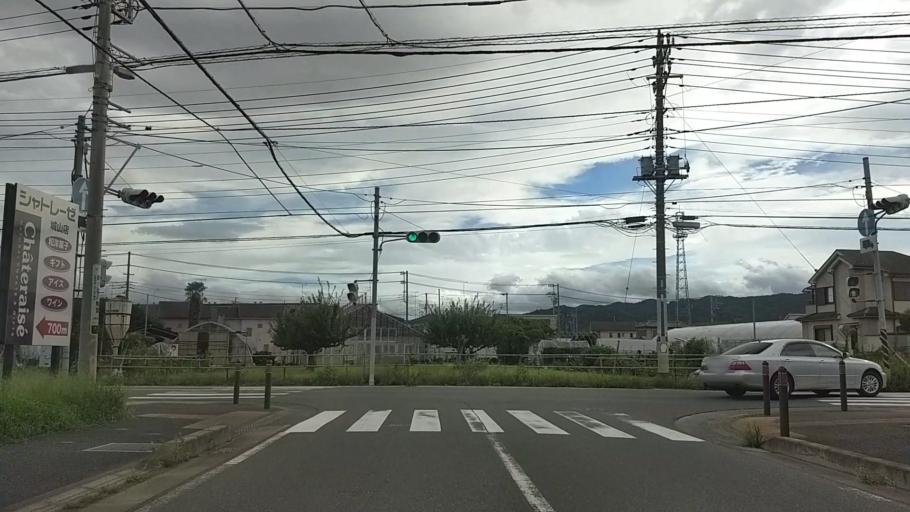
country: JP
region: Tokyo
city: Hachioji
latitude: 35.5887
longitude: 139.3121
